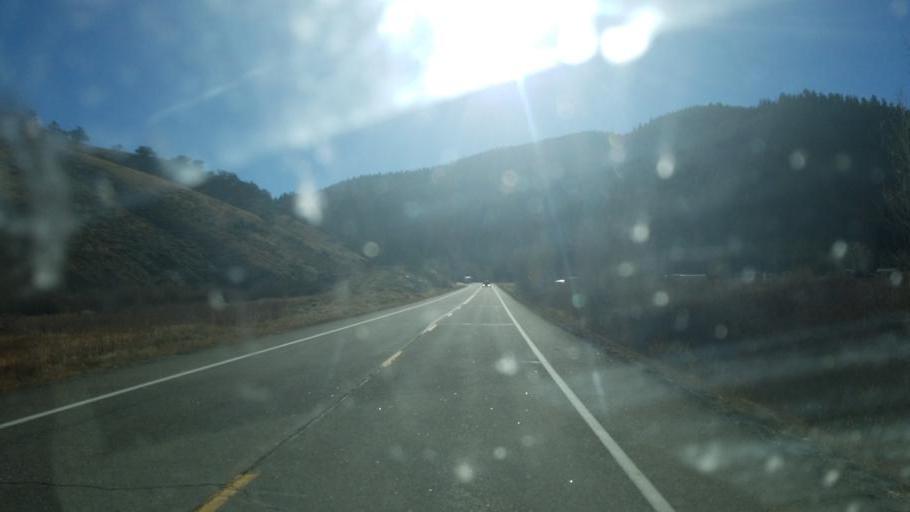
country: US
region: Colorado
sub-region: Saguache County
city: Saguache
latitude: 38.3912
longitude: -106.4559
